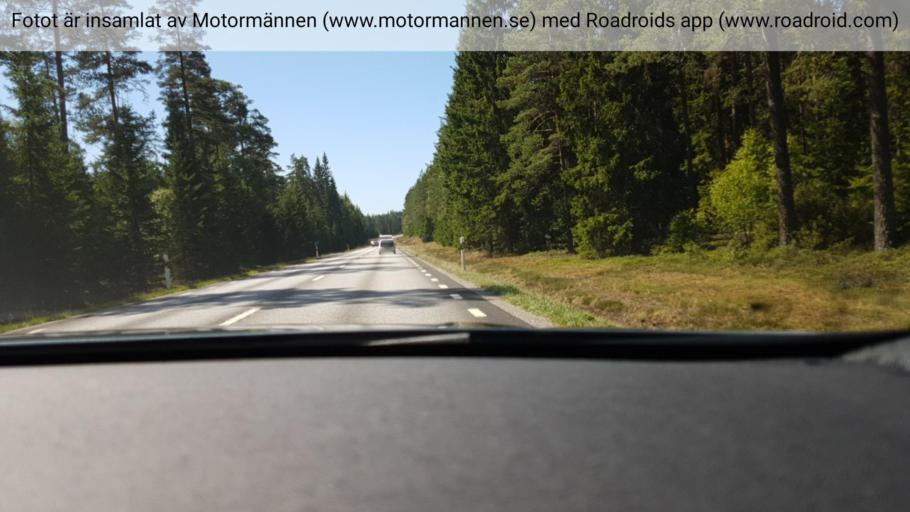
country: SE
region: Joenkoeping
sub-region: Gnosjo Kommun
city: Gnosjoe
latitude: 57.5750
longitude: 13.7137
